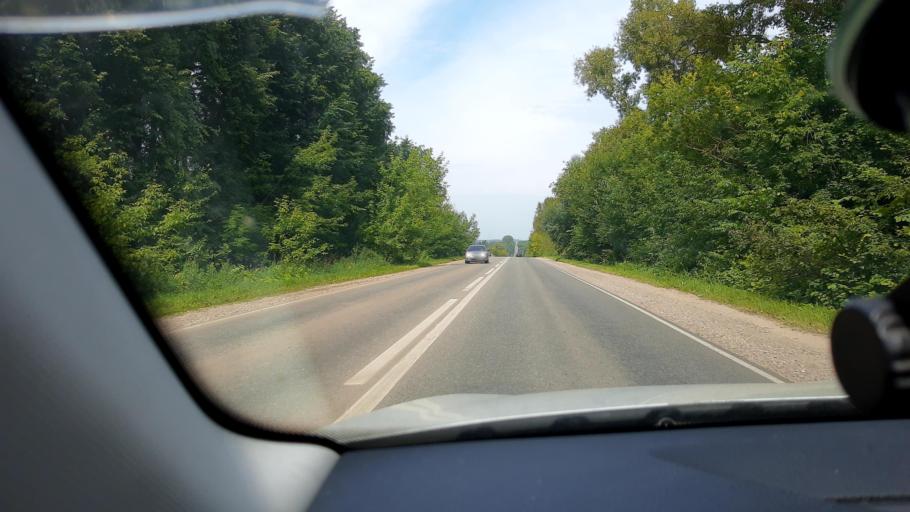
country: RU
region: Tula
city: Zaokskiy
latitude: 54.7668
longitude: 37.4365
